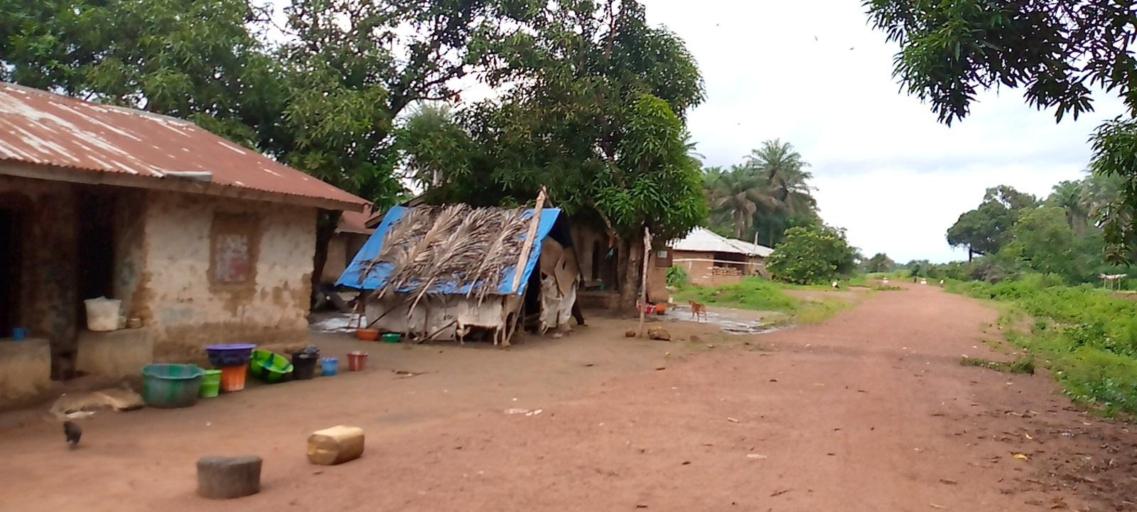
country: SL
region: Northern Province
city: Port Loko
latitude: 8.7207
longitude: -12.7885
